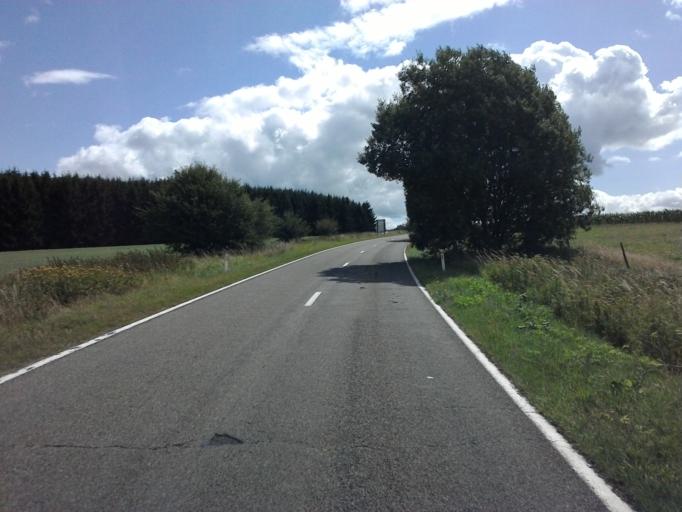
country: BE
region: Wallonia
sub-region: Province du Luxembourg
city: Habay-la-Vieille
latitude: 49.7792
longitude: 5.6125
